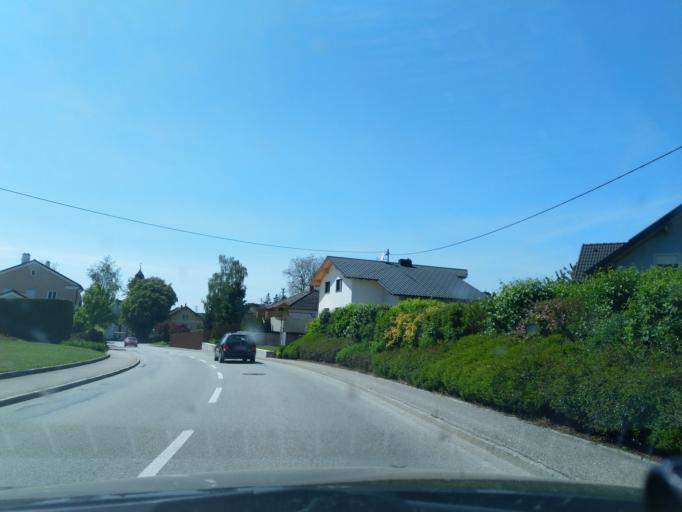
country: DE
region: Bavaria
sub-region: Lower Bavaria
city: Bad Fussing
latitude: 48.2773
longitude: 13.3761
